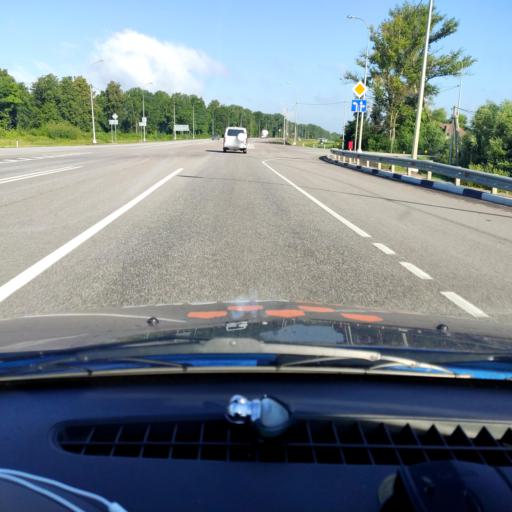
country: RU
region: Orjol
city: Orel
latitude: 52.8599
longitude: 36.1983
